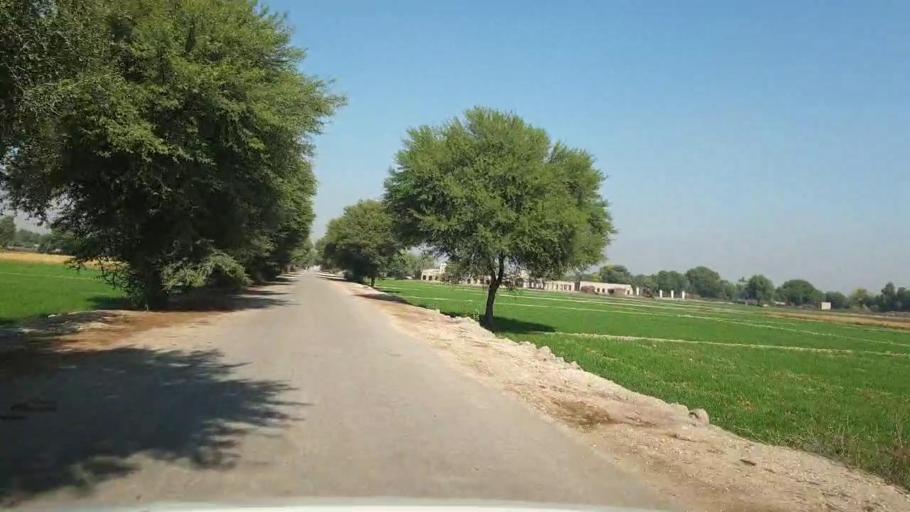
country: PK
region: Sindh
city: Johi
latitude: 26.6639
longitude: 67.7054
